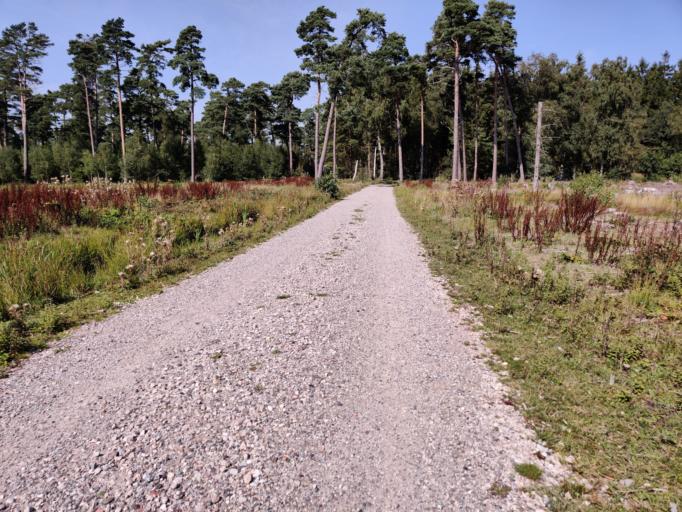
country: DK
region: Zealand
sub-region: Guldborgsund Kommune
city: Nykobing Falster
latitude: 54.6358
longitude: 11.9577
